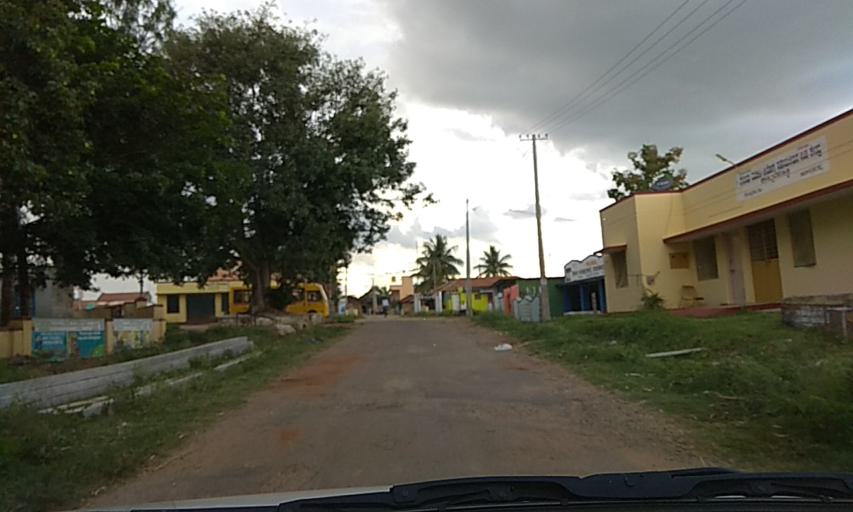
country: IN
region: Karnataka
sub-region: Chamrajnagar
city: Gundlupet
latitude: 11.8712
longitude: 76.7242
